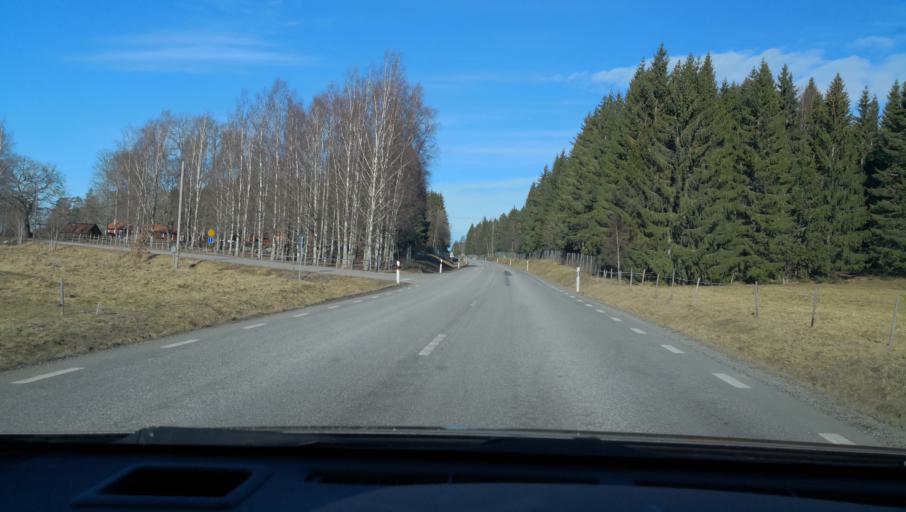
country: SE
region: Uppsala
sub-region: Uppsala Kommun
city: Vattholma
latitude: 60.0290
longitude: 17.7499
